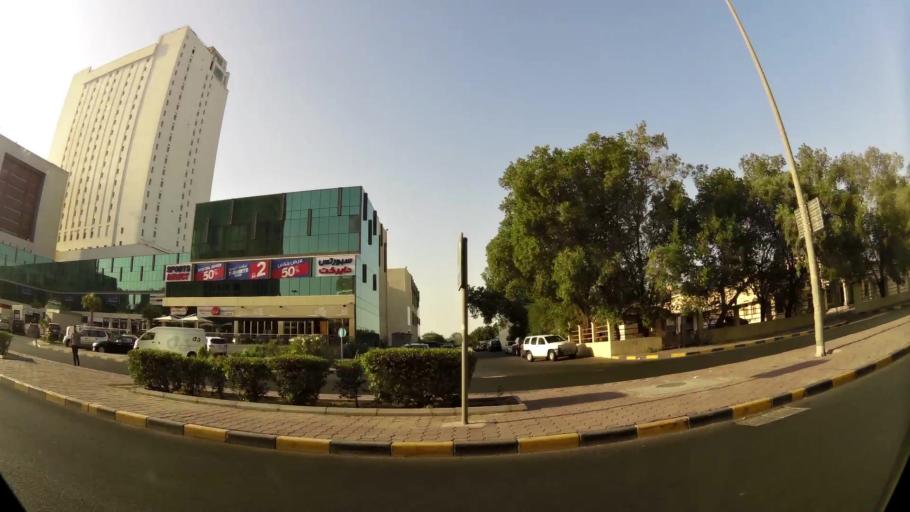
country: KW
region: Muhafazat Hawalli
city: As Salimiyah
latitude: 29.3427
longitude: 48.0780
